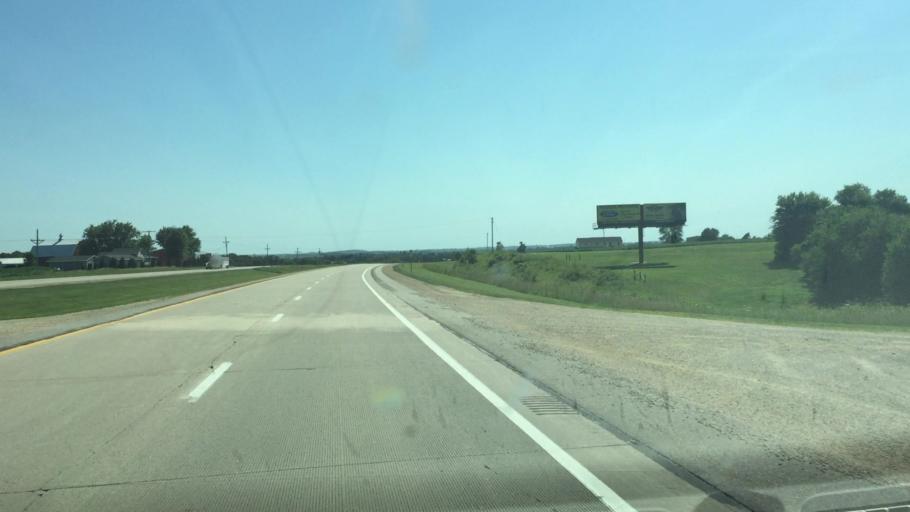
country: US
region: Iowa
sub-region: Jones County
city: Monticello
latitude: 42.2656
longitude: -91.1461
